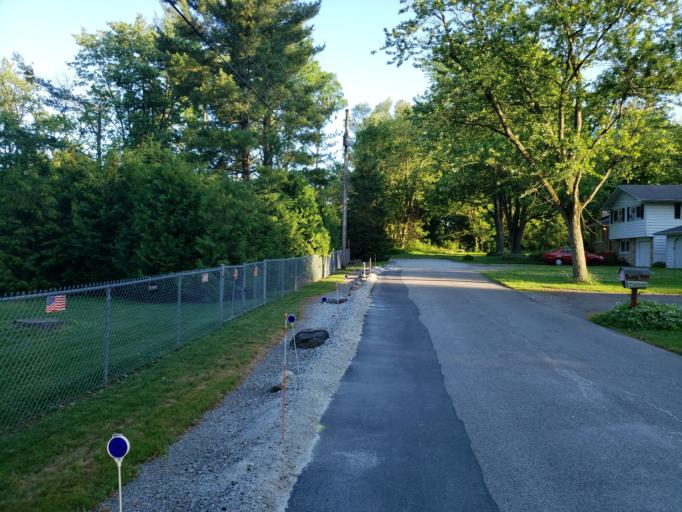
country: US
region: Indiana
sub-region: Lake County
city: Cedar Lake
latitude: 41.3353
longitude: -87.4324
